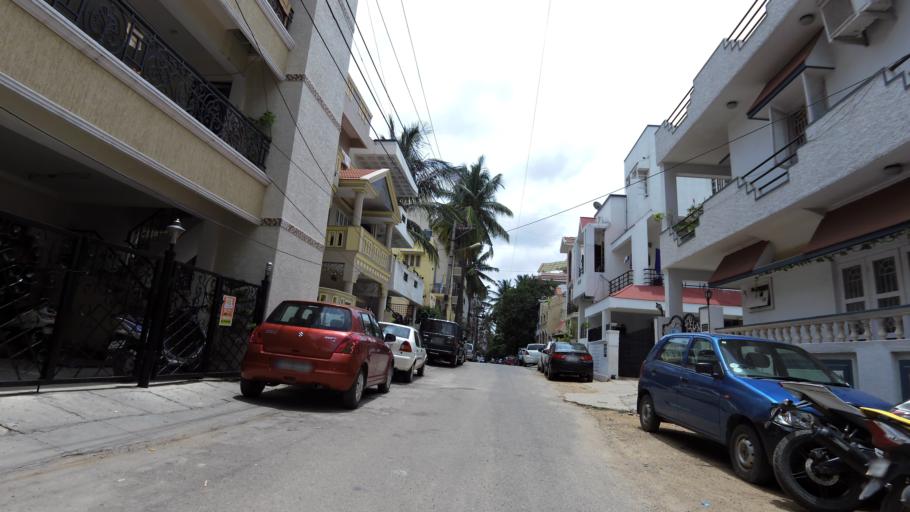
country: IN
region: Karnataka
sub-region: Bangalore Urban
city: Bangalore
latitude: 13.0044
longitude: 77.6286
